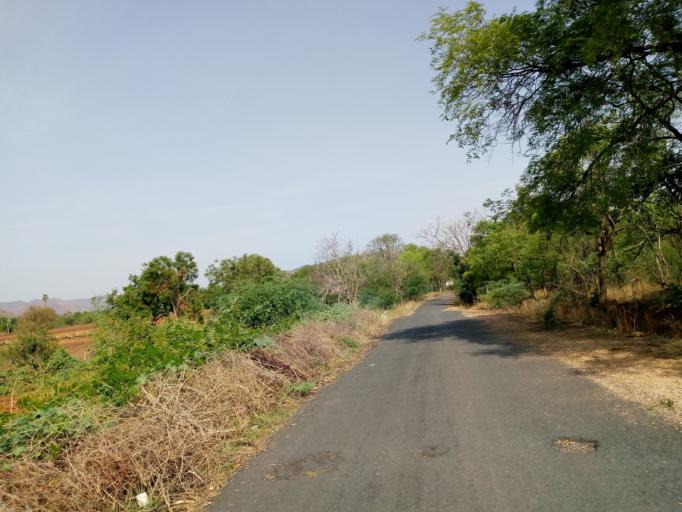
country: IN
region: Andhra Pradesh
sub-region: Prakasam
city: Cumbum
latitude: 15.7152
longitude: 79.0789
